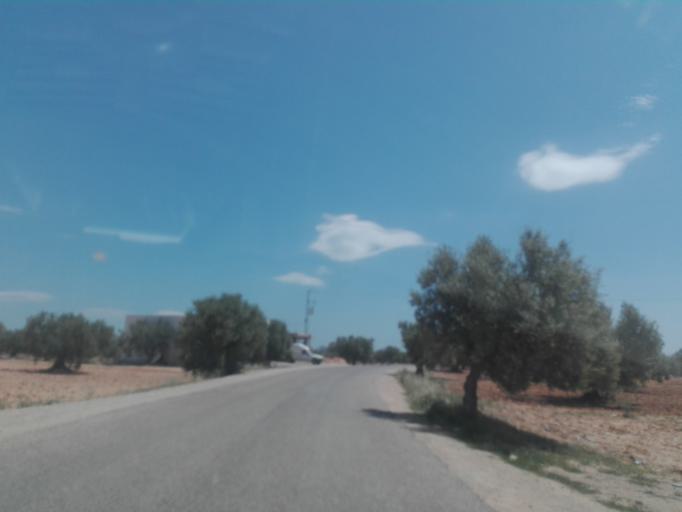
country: TN
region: Safaqis
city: Sfax
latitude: 34.6245
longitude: 10.6042
